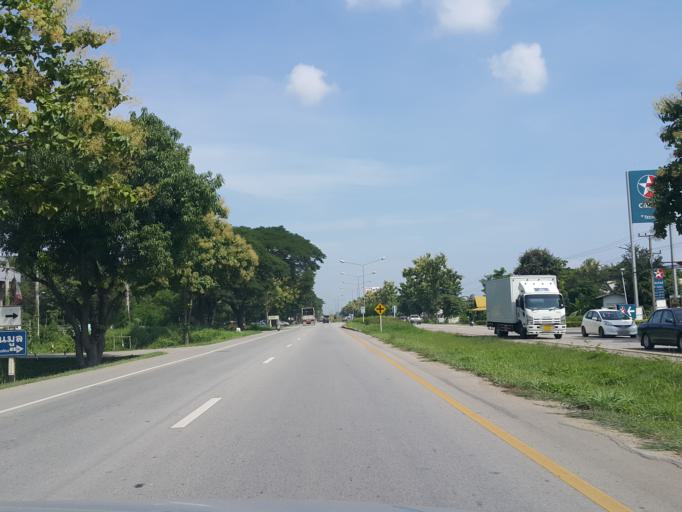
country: TH
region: Chiang Mai
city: Saraphi
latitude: 18.7112
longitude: 99.0449
